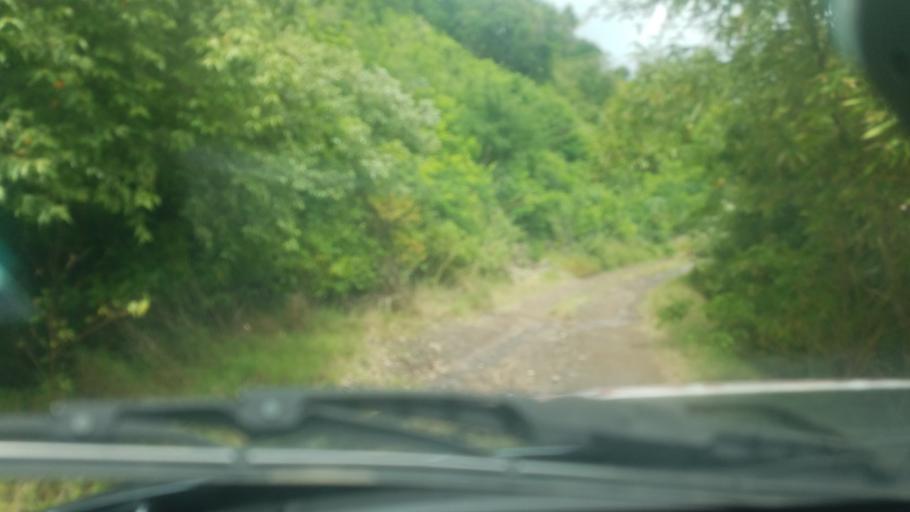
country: LC
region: Gros-Islet
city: Gros Islet
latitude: 14.0408
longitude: -60.9055
